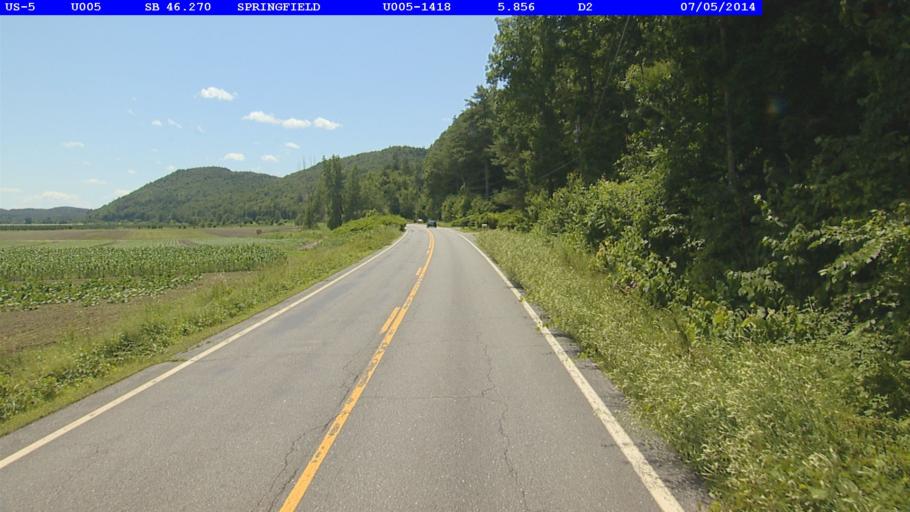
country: US
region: New Hampshire
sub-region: Sullivan County
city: Charlestown
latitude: 43.2970
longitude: -72.4080
